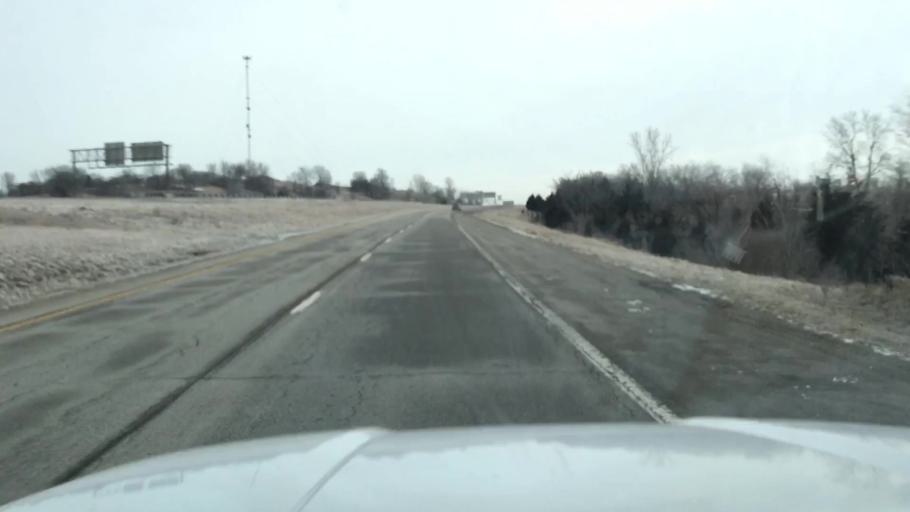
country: US
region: Missouri
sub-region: Andrew County
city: Savannah
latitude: 39.8881
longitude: -94.8567
